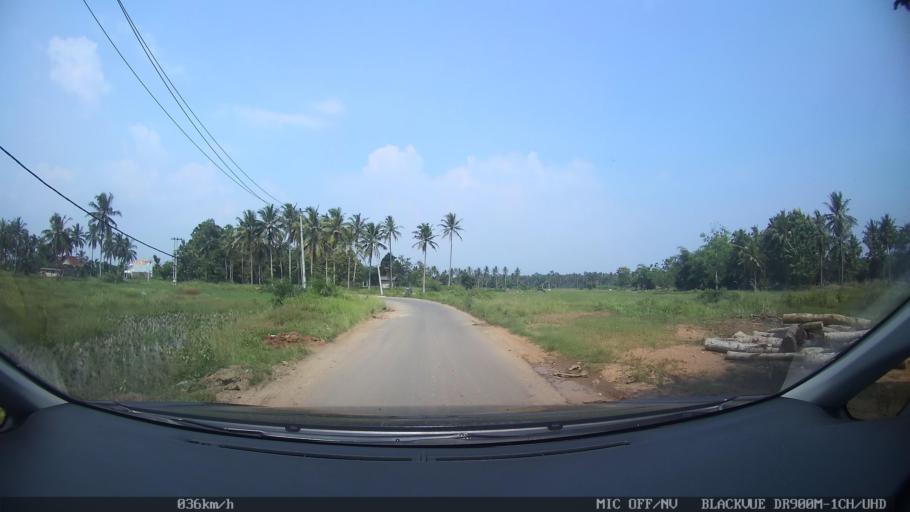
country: ID
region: Lampung
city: Natar
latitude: -5.3064
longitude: 105.2340
